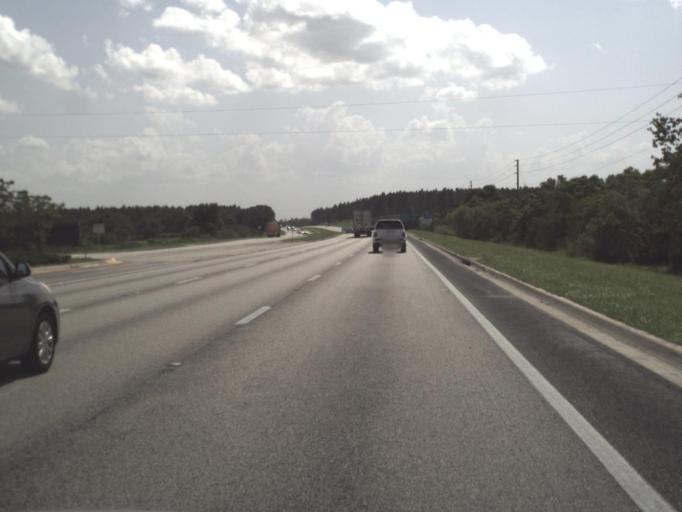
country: US
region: Florida
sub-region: Polk County
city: Haines City
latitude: 28.1005
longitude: -81.6459
